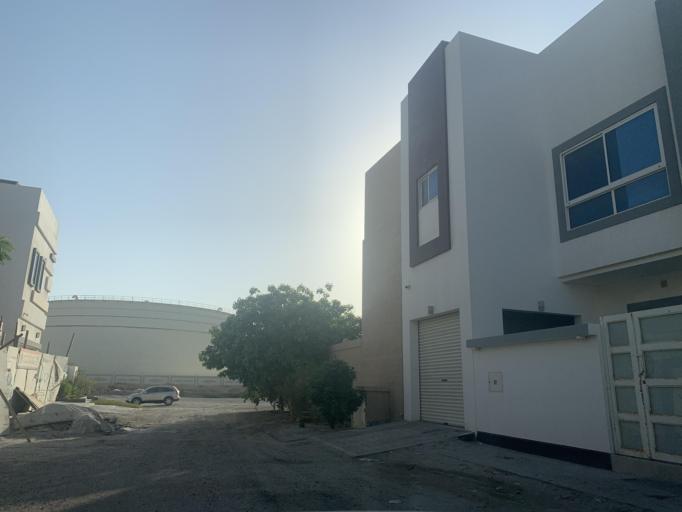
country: BH
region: Manama
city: Jidd Hafs
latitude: 26.2091
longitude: 50.5280
